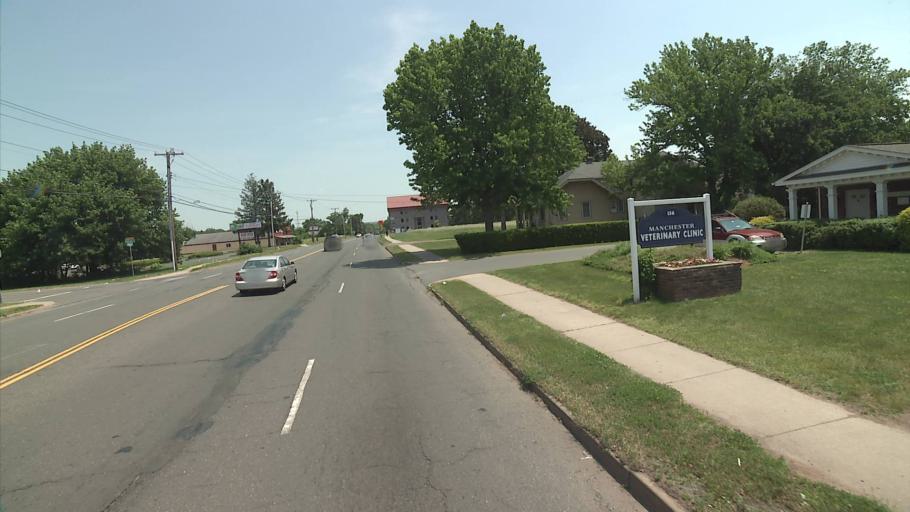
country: US
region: Connecticut
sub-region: Hartford County
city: Manchester
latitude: 41.7672
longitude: -72.5675
